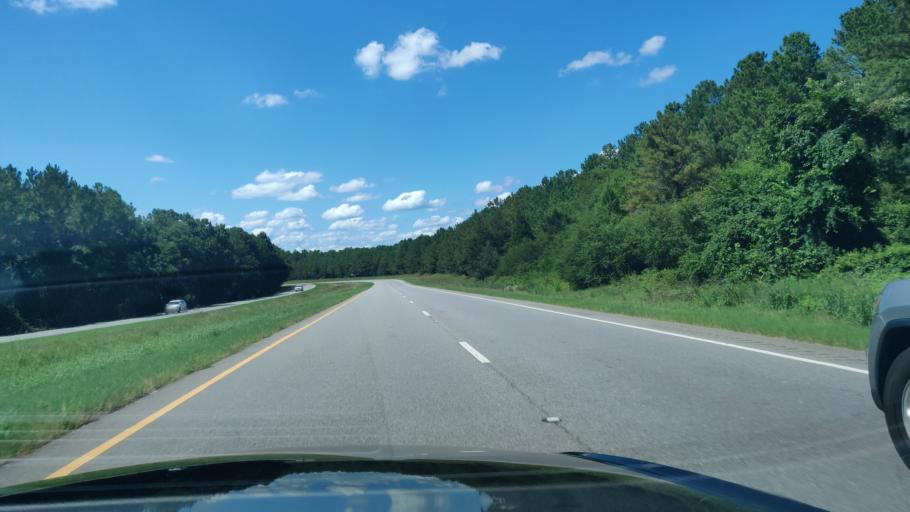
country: US
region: Georgia
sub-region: Terrell County
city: Dawson
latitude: 31.8635
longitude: -84.4836
